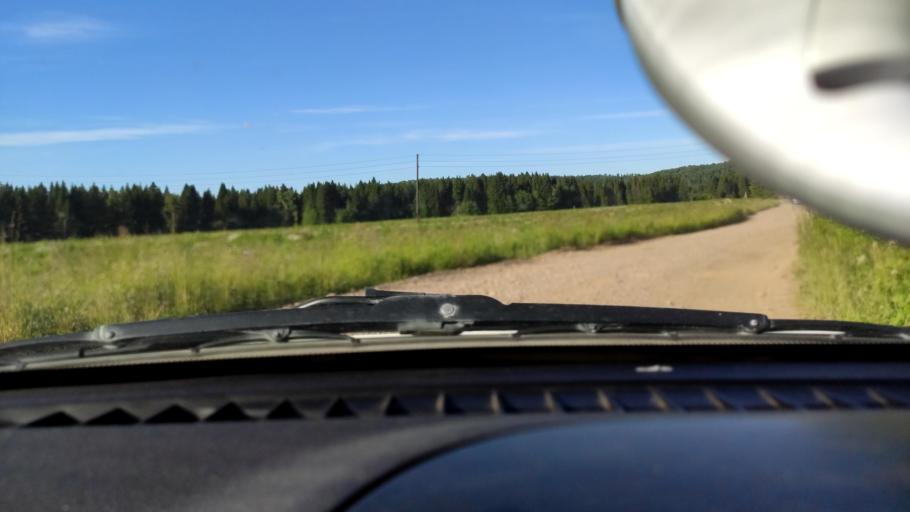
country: RU
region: Perm
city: Bershet'
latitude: 57.6950
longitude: 56.4021
